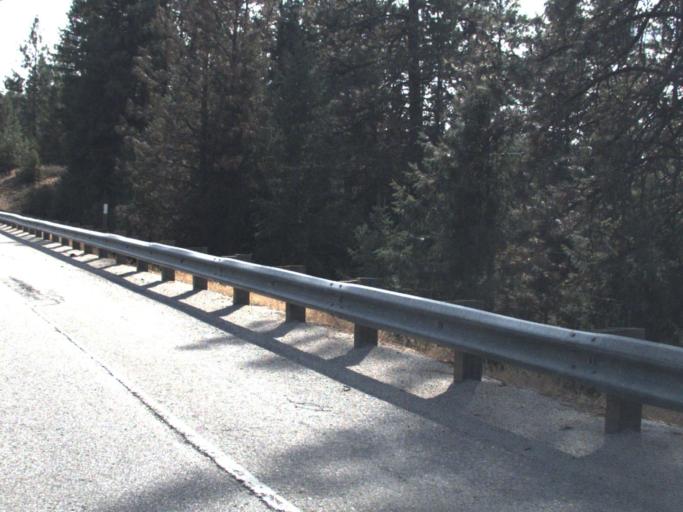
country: US
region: Washington
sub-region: Stevens County
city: Chewelah
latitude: 48.1490
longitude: -117.6871
